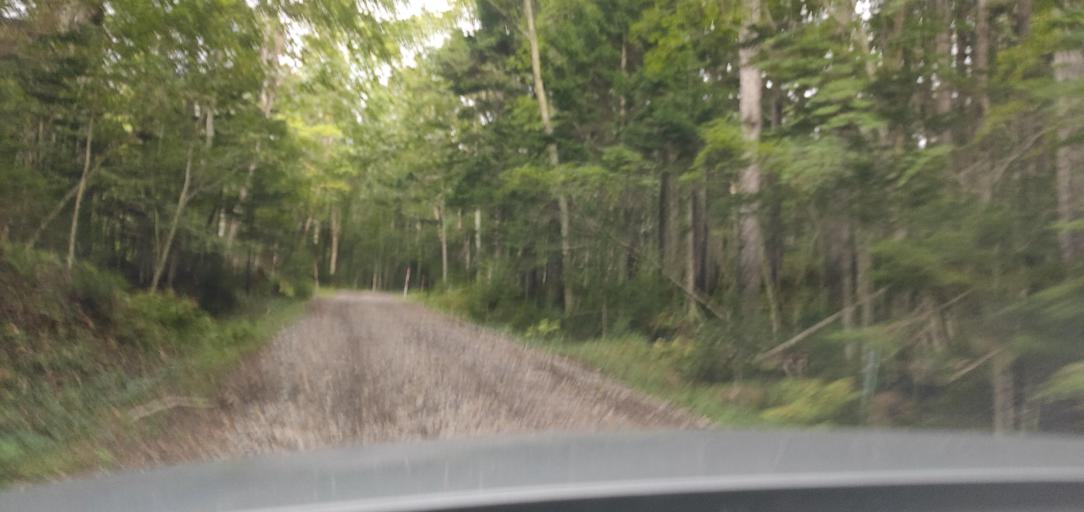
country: JP
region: Hokkaido
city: Kitami
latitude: 43.3701
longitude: 143.9479
